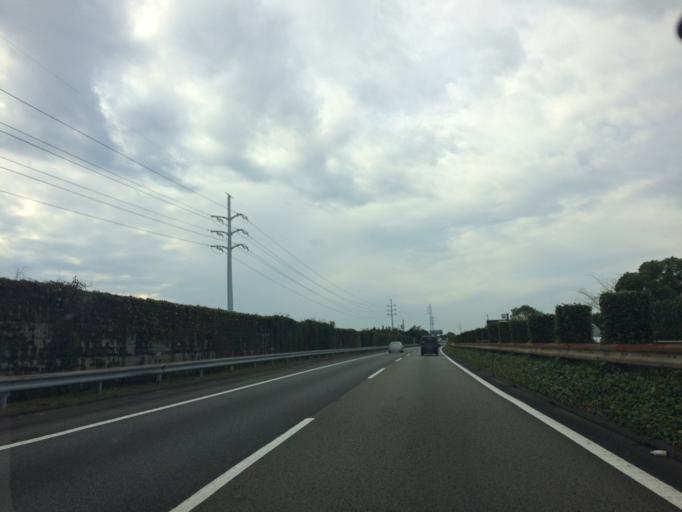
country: JP
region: Shizuoka
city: Fujieda
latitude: 34.8383
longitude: 138.2807
